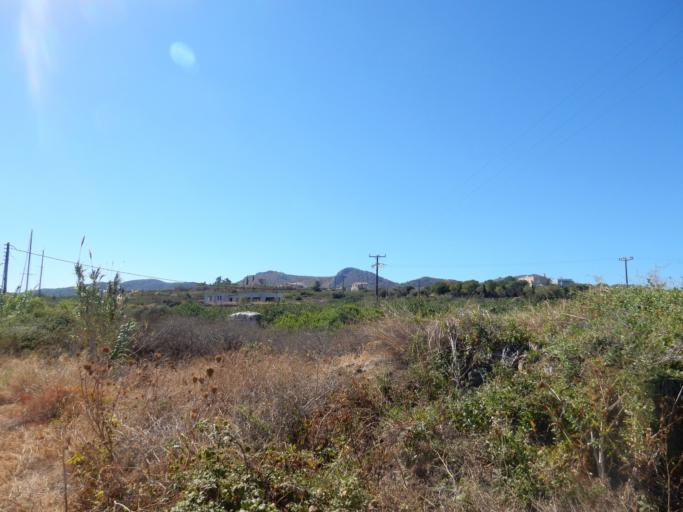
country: GR
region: Attica
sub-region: Nomos Piraios
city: Kypseli
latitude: 37.7703
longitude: 23.4578
